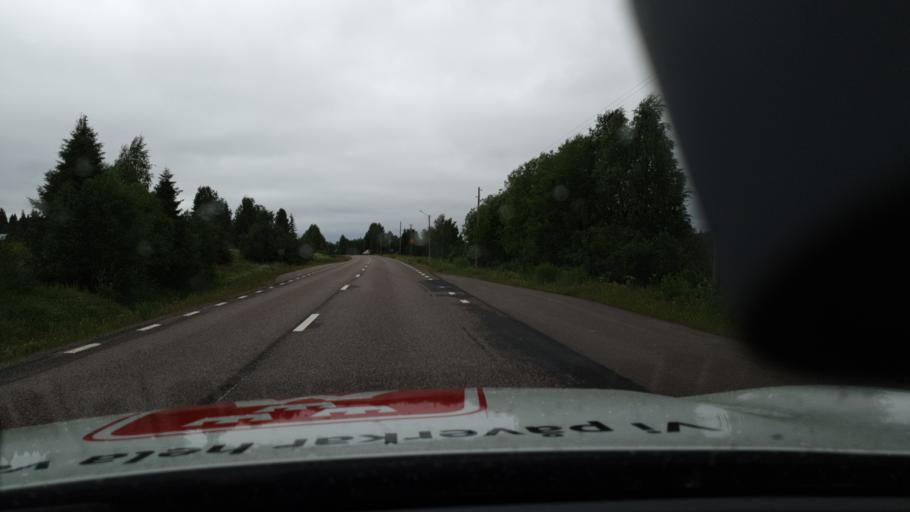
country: FI
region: Lapland
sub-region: Torniolaakso
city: Pello
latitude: 66.9396
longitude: 23.8513
